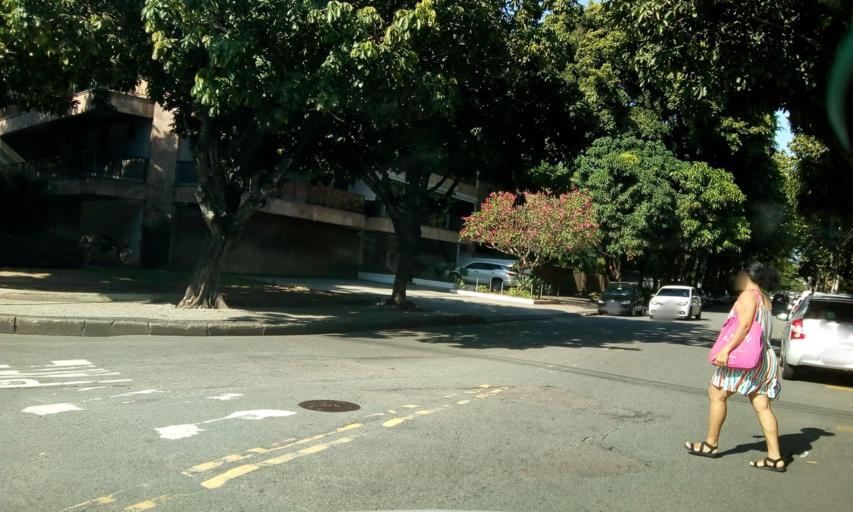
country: BR
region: Rio de Janeiro
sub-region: Rio De Janeiro
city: Rio de Janeiro
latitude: -23.0110
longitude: -43.3098
